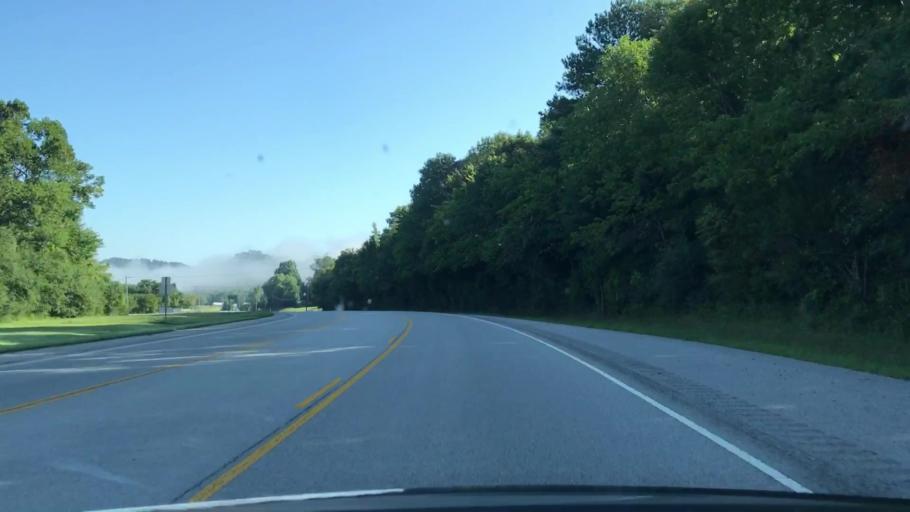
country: US
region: Tennessee
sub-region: Jackson County
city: Gainesboro
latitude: 36.3792
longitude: -85.6390
